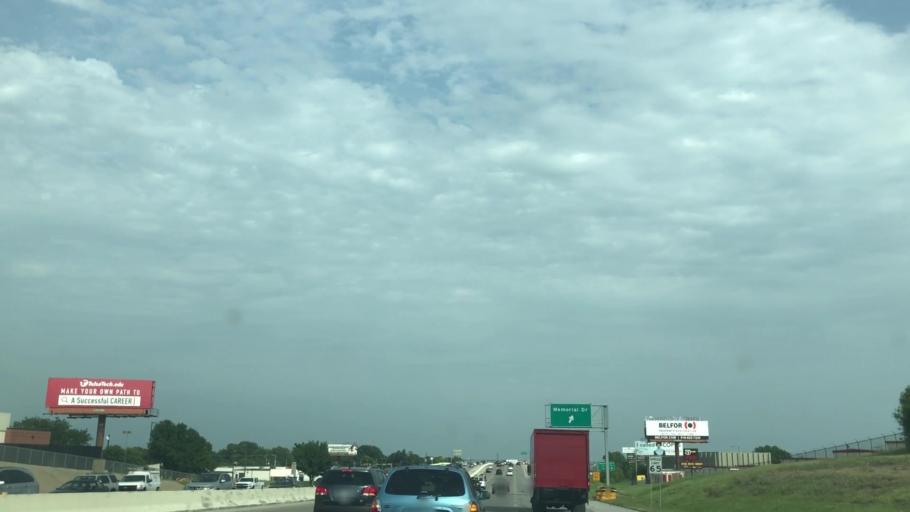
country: US
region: Oklahoma
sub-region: Tulsa County
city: Tulsa
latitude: 36.1110
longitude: -95.8917
